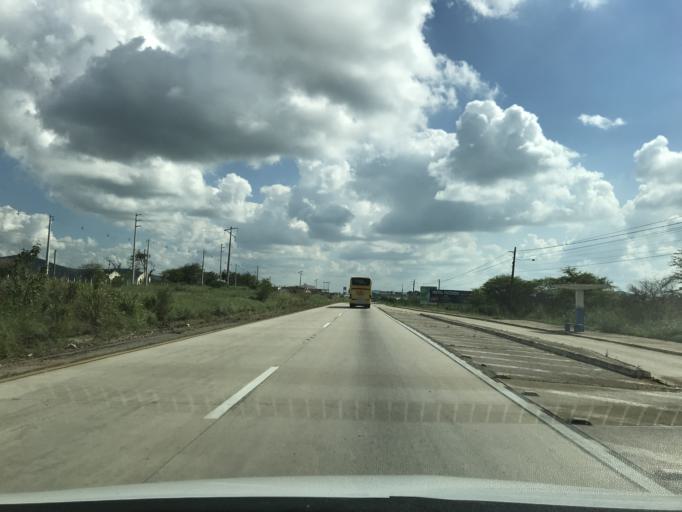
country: BR
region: Pernambuco
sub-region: Gravata
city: Gravata
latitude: -8.2170
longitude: -35.6531
